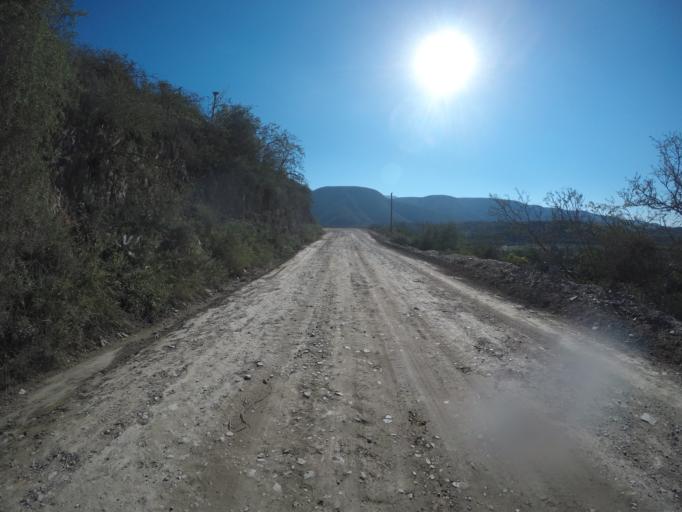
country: ZA
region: Eastern Cape
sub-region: Cacadu District Municipality
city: Kruisfontein
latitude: -33.6650
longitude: 24.5678
